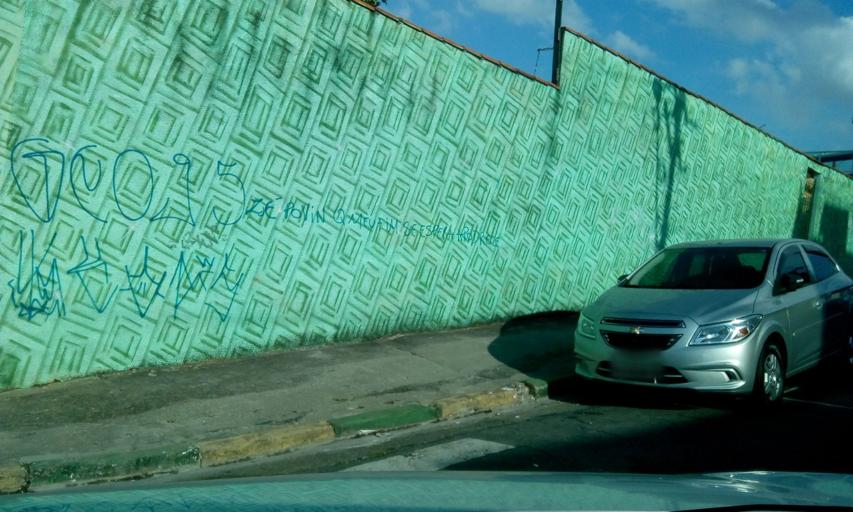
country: BR
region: Sao Paulo
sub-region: Sao Paulo
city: Sao Paulo
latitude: -23.4795
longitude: -46.6749
